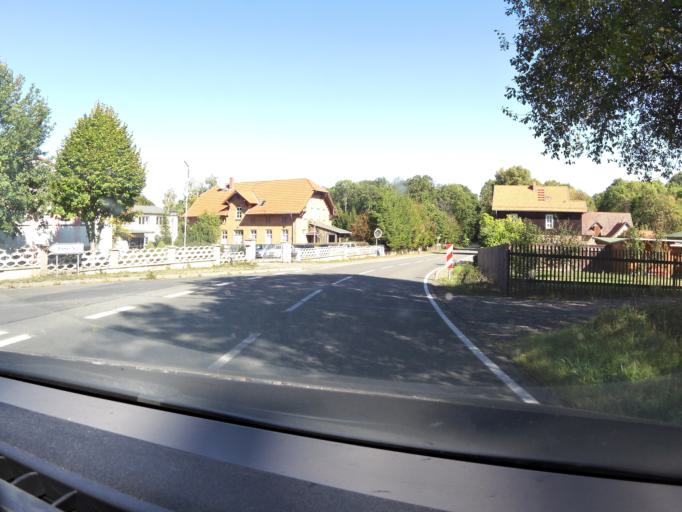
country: DE
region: Saxony-Anhalt
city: Gernrode
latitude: 51.7103
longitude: 11.1328
